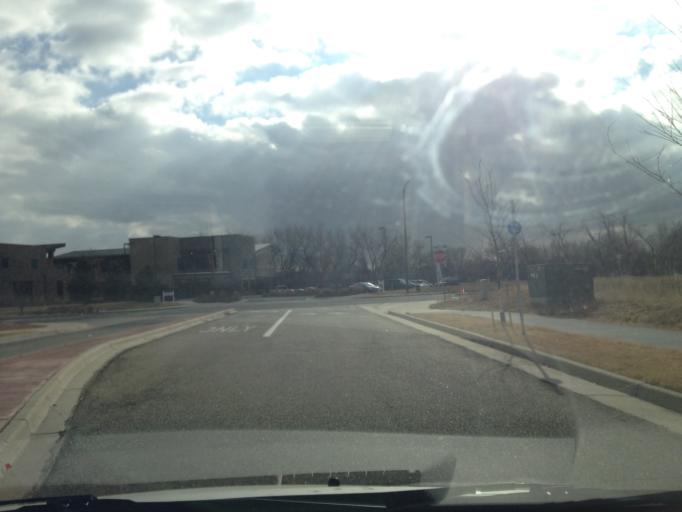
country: US
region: Colorado
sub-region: Boulder County
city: Lafayette
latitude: 39.9818
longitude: -105.0928
